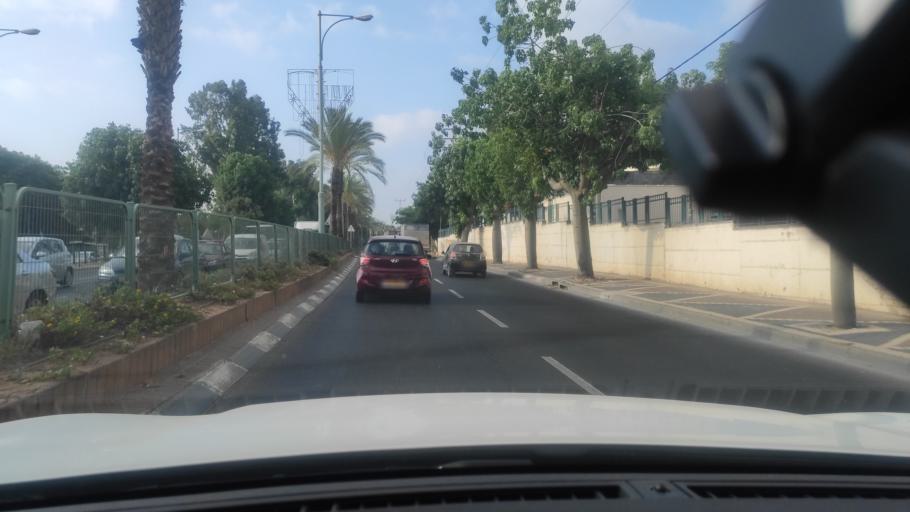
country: IL
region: Central District
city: Petah Tiqwa
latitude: 32.0944
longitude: 34.9019
